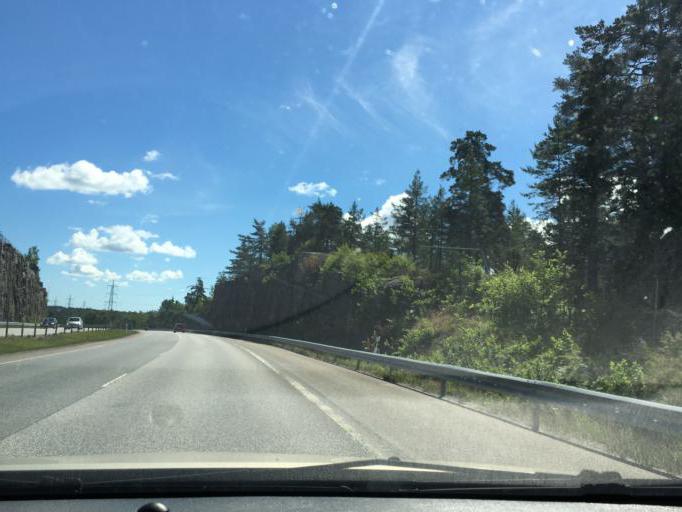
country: SE
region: Stockholm
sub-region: Nacka Kommun
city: Alta
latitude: 59.2932
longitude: 18.2099
